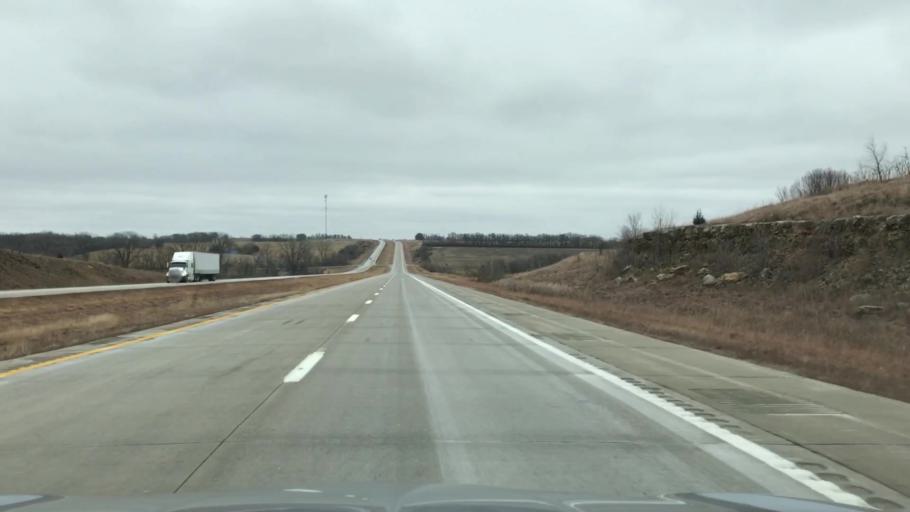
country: US
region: Missouri
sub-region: Caldwell County
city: Hamilton
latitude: 39.7347
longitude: -93.7856
